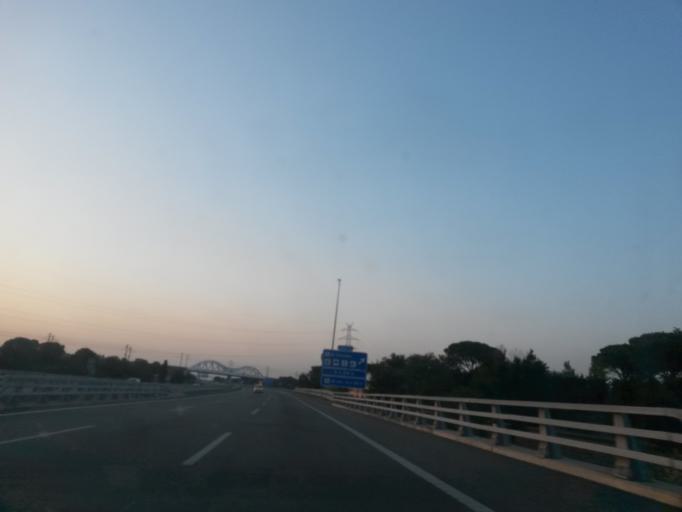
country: ES
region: Catalonia
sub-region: Provincia de Girona
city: Vilobi d'Onyar
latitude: 41.8959
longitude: 2.7752
